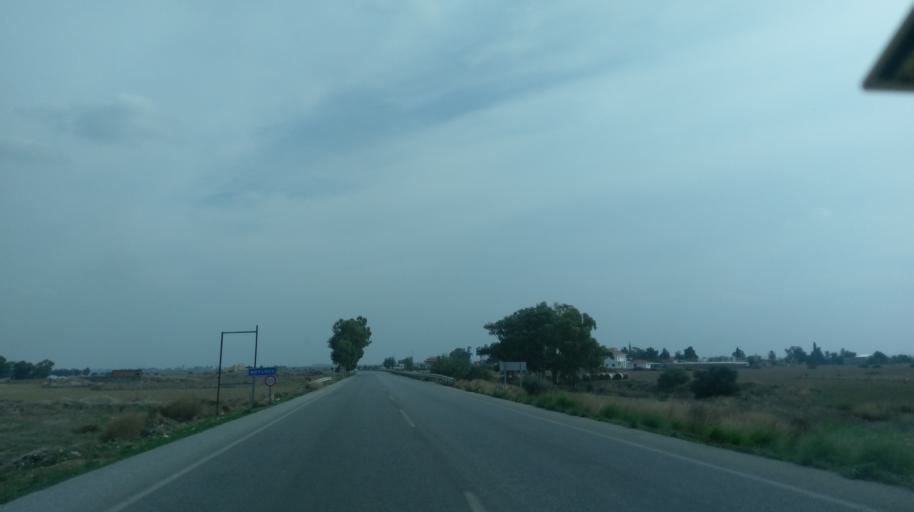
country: CY
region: Ammochostos
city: Lefkonoiko
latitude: 35.2578
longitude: 33.6798
